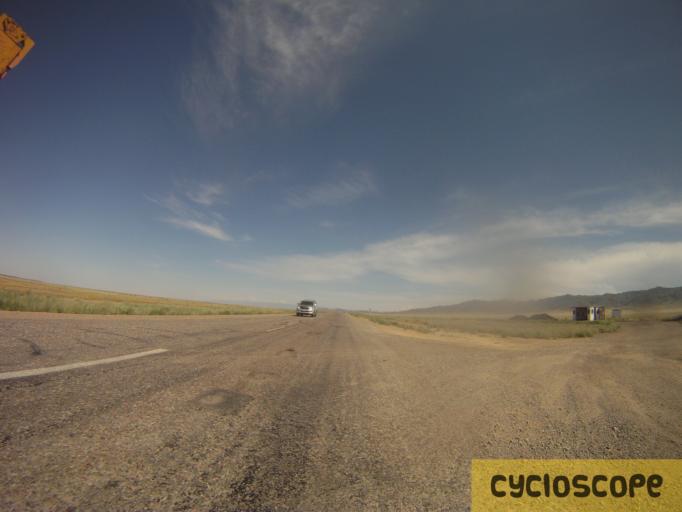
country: KZ
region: Almaty Oblysy
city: Kegen
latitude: 43.3938
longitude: 78.8200
